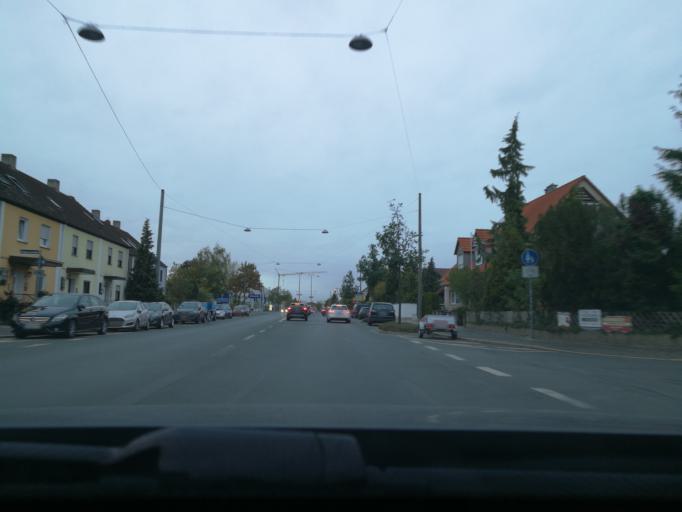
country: DE
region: Bavaria
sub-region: Regierungsbezirk Mittelfranken
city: Furth
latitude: 49.4762
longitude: 11.0151
